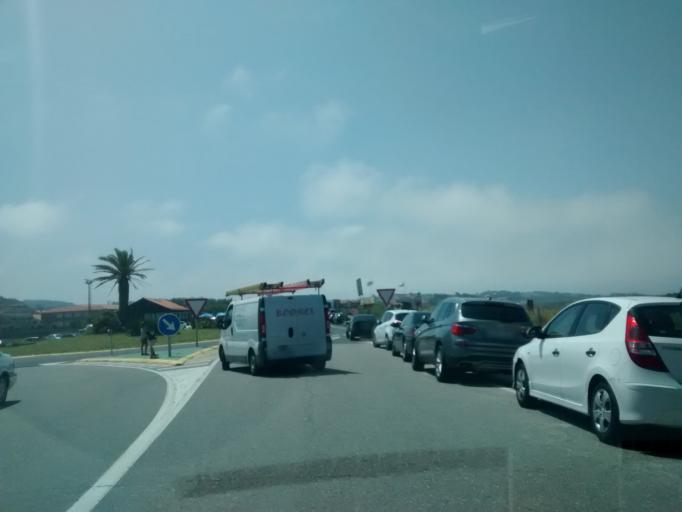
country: ES
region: Galicia
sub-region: Provincia de Pontevedra
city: O Grove
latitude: 42.4400
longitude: -8.8714
